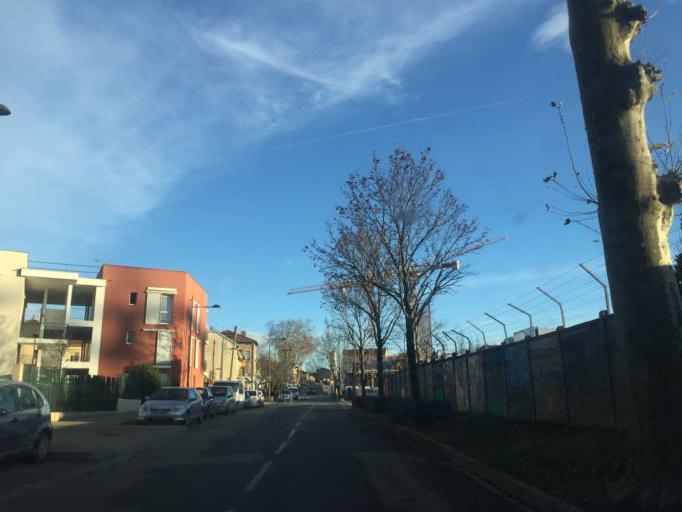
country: FR
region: Rhone-Alpes
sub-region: Departement du Rhone
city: Sathonay-Camp
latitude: 45.8257
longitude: 4.8719
